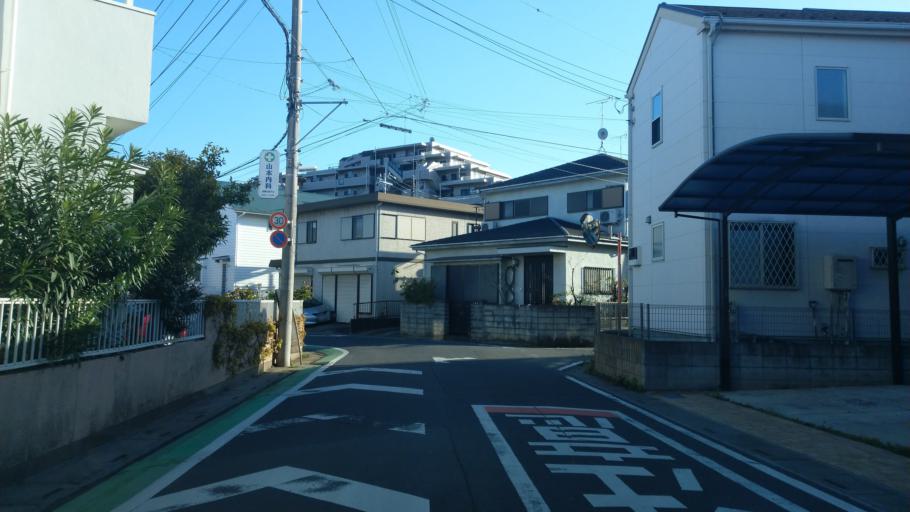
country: JP
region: Saitama
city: Ageoshimo
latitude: 35.9187
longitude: 139.5723
